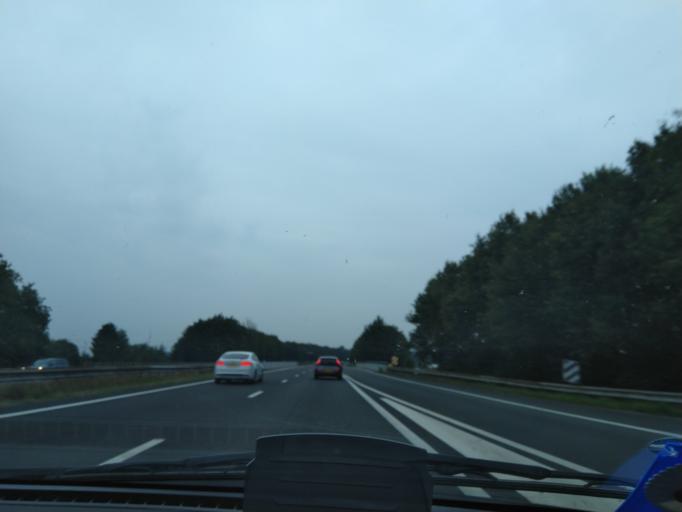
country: NL
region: Drenthe
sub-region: Gemeente Assen
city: Assen
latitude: 52.9964
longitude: 6.5258
